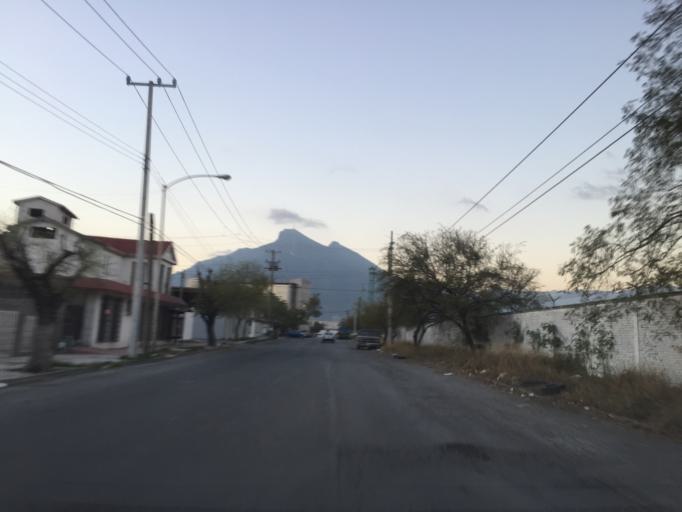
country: MX
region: Nuevo Leon
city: Guadalupe
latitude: 25.6980
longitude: -100.2233
